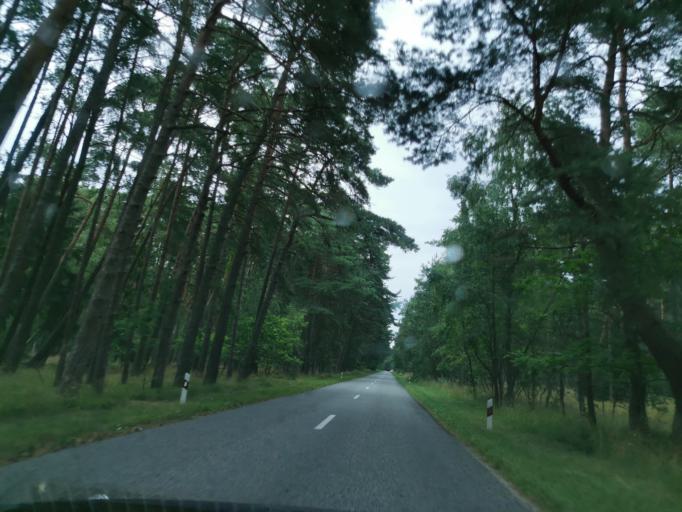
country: LT
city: Nida
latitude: 55.1349
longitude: 20.7963
